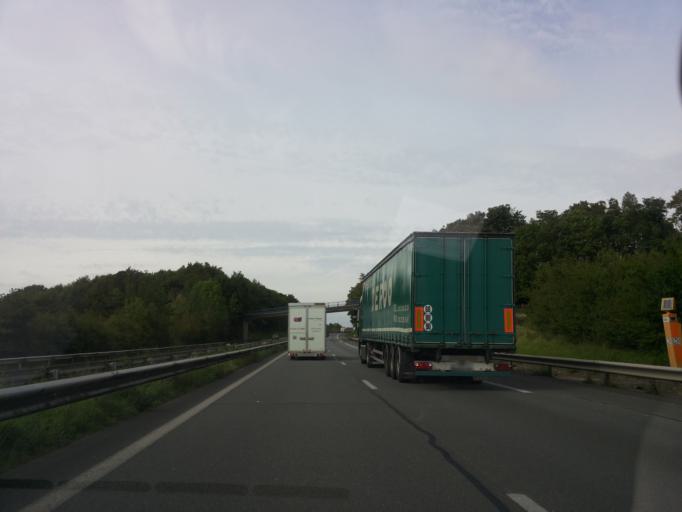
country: FR
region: Nord-Pas-de-Calais
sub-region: Departement du Pas-de-Calais
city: Norrent-Fontes
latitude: 50.5617
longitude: 2.4040
